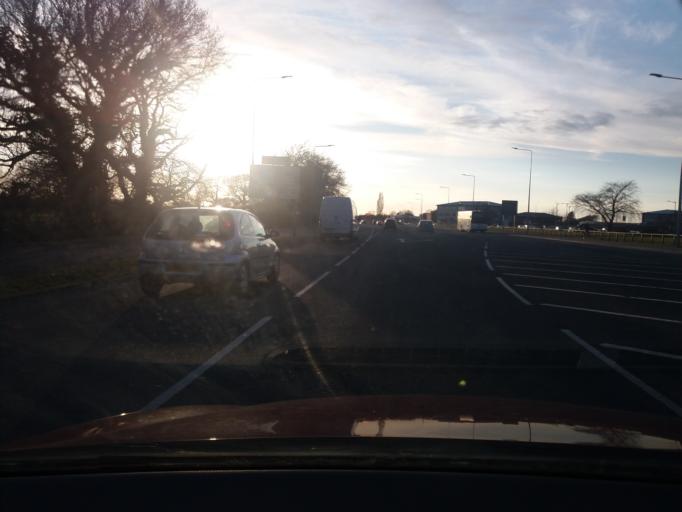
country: GB
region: England
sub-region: Lancashire
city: Euxton
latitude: 53.6716
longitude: -2.6600
